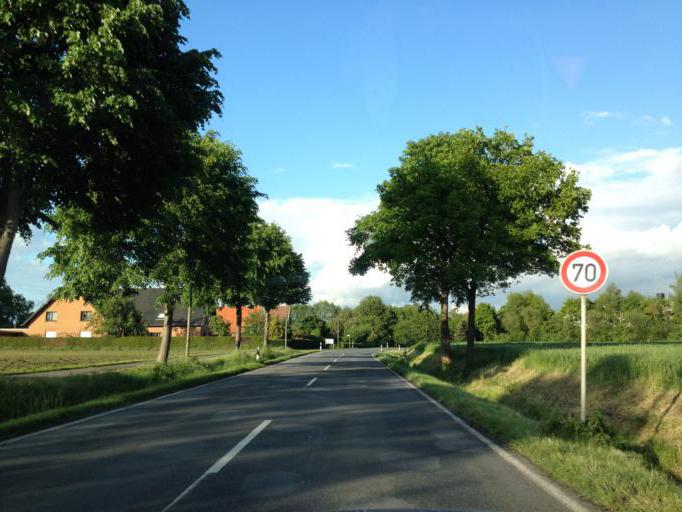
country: DE
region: North Rhine-Westphalia
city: Rietberg
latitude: 51.8601
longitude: 8.4228
